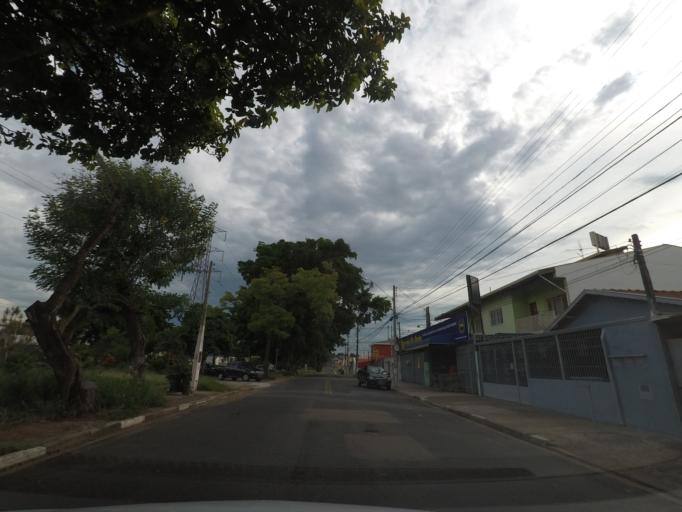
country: BR
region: Sao Paulo
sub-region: Campinas
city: Campinas
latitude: -22.8834
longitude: -47.1270
